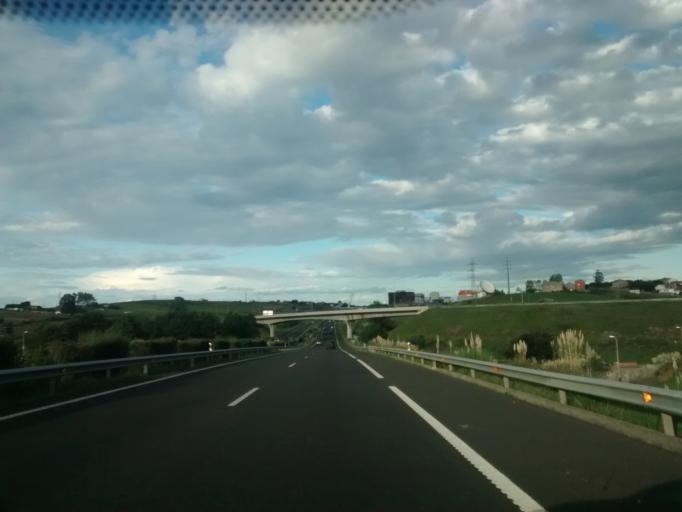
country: ES
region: Cantabria
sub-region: Provincia de Cantabria
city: Santa Cruz de Bezana
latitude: 43.4473
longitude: -3.8846
